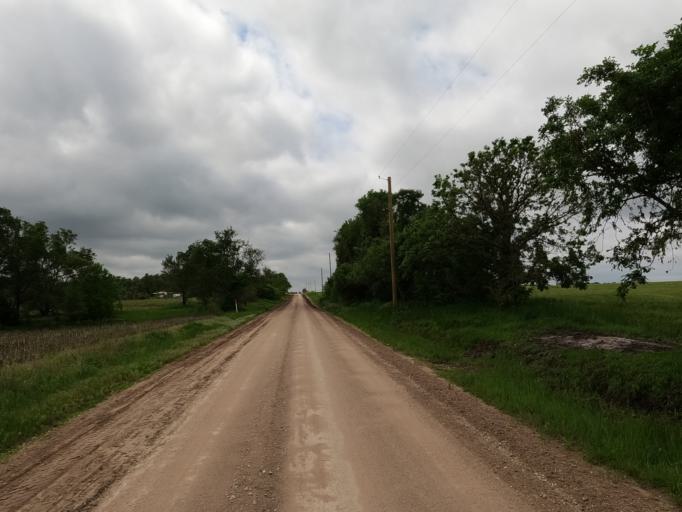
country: US
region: Kansas
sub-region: McPherson County
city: McPherson
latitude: 38.3023
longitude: -97.6120
